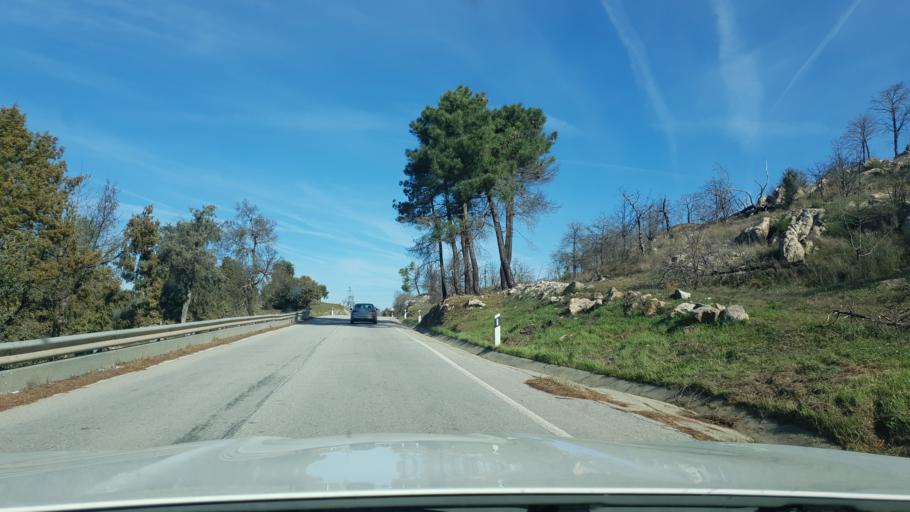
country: PT
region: Braganca
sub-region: Torre de Moncorvo
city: Torre de Moncorvo
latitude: 41.1834
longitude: -7.0235
